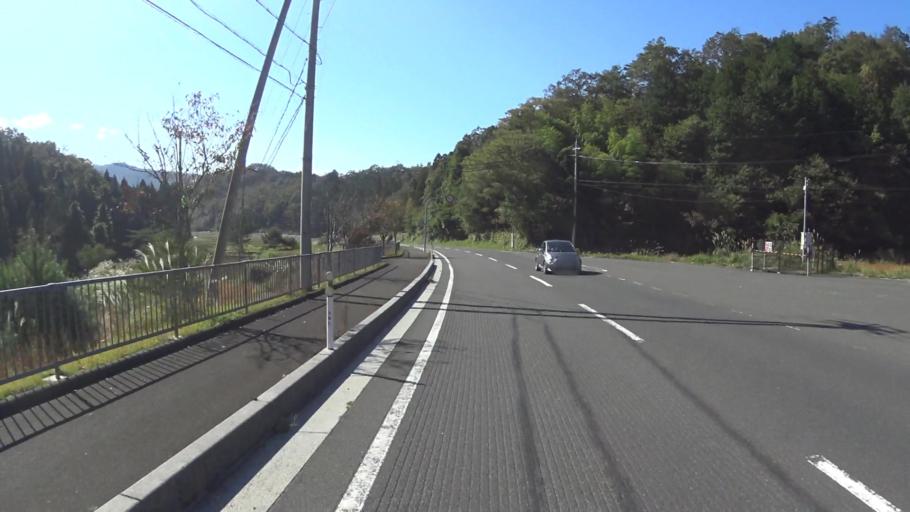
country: JP
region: Hyogo
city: Toyooka
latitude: 35.5763
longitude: 134.9910
